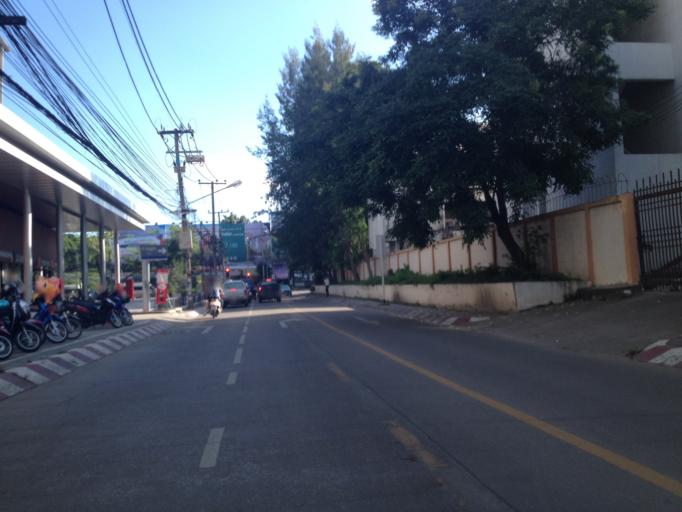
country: TH
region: Chiang Mai
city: Chiang Mai
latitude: 18.7908
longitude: 98.9706
